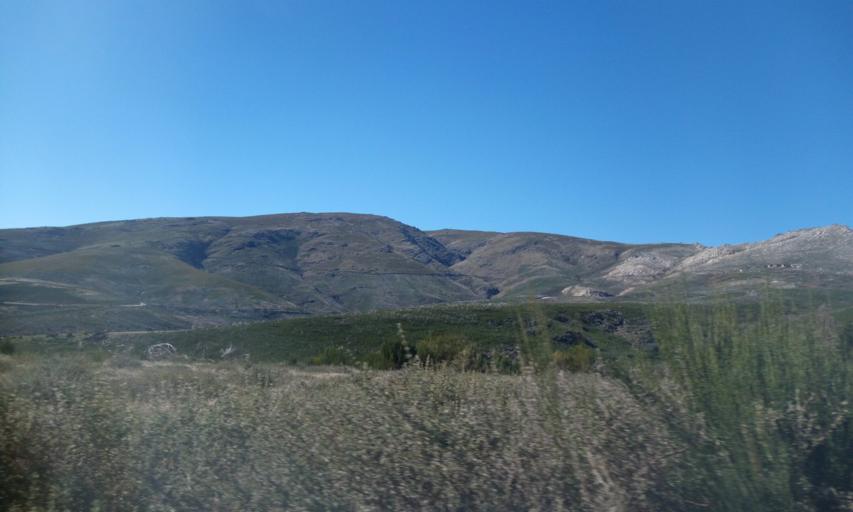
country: PT
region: Guarda
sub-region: Manteigas
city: Manteigas
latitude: 40.4684
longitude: -7.5027
